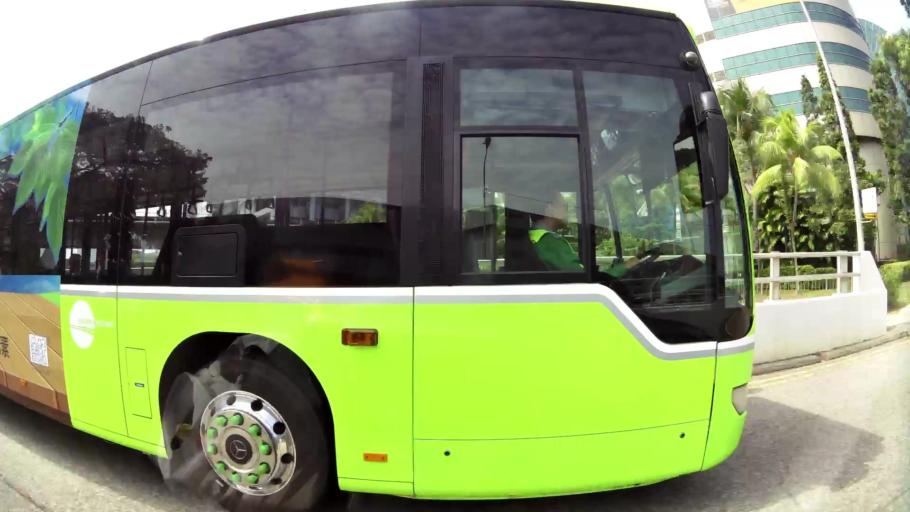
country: SG
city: Singapore
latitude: 1.3290
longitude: 103.7496
